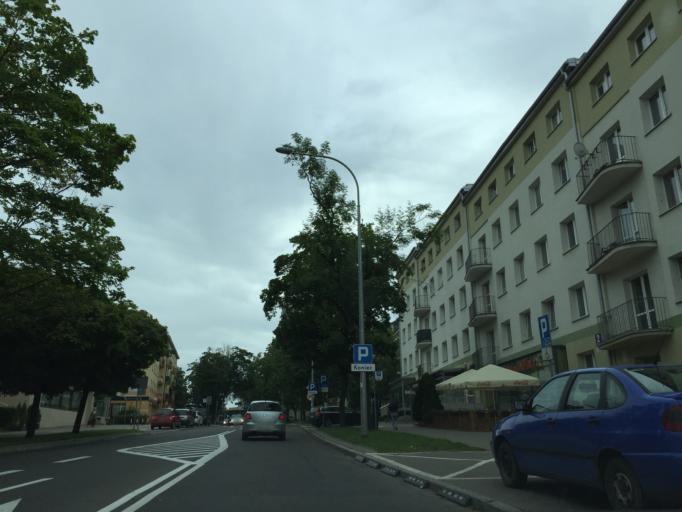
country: PL
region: Podlasie
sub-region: Bialystok
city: Bialystok
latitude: 53.1332
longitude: 23.1514
